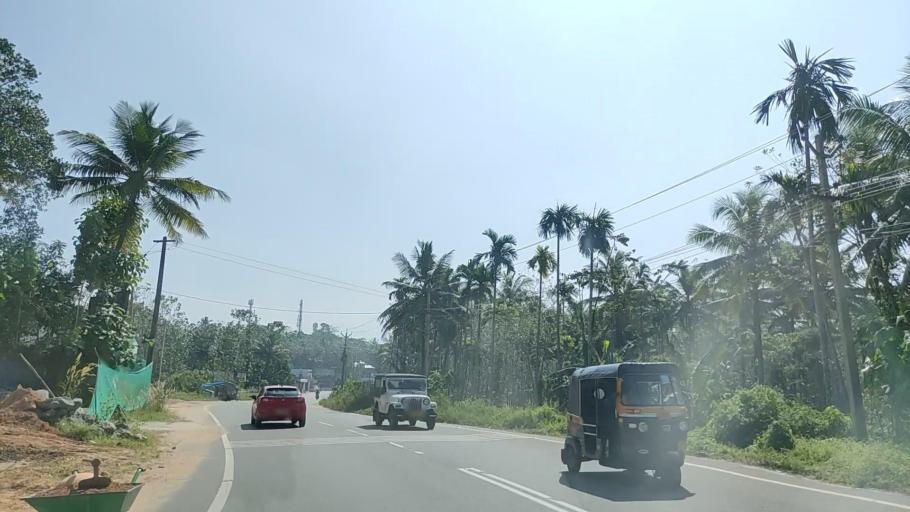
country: IN
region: Kerala
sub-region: Kollam
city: Punalur
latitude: 8.9102
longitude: 77.0508
